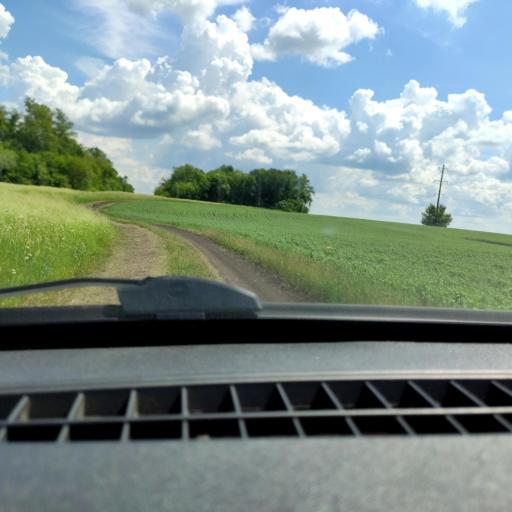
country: RU
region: Bashkortostan
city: Kabakovo
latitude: 54.5178
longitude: 56.0899
